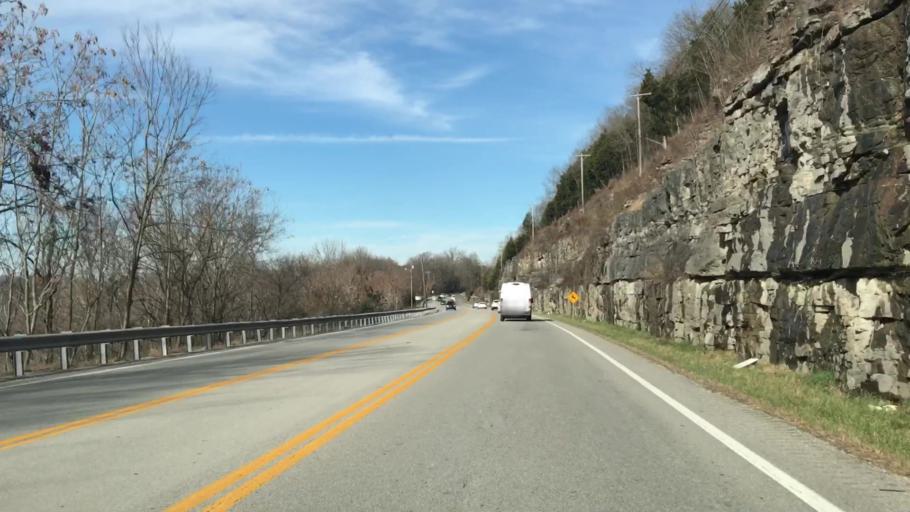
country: US
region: Kentucky
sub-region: Pulaski County
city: Somerset
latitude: 36.9783
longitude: -84.5942
